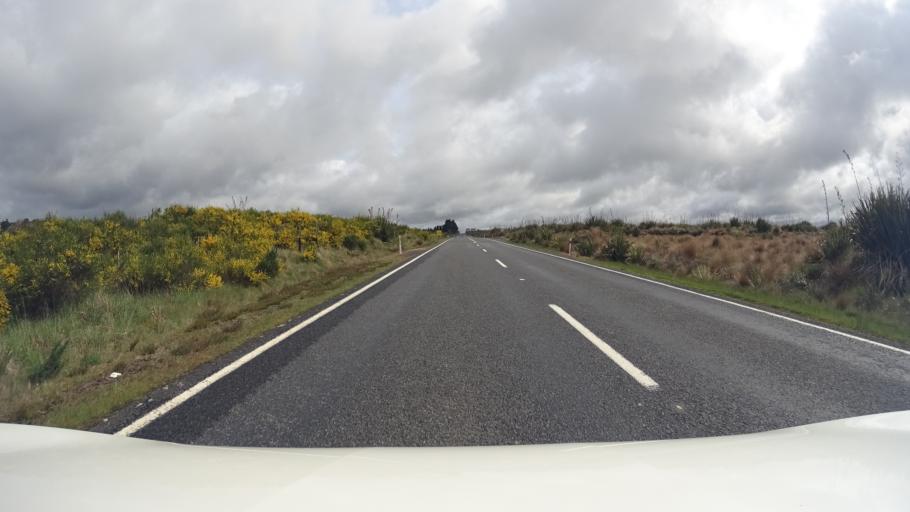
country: NZ
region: Manawatu-Wanganui
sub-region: Ruapehu District
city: Waiouru
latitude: -39.1869
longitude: 175.4019
